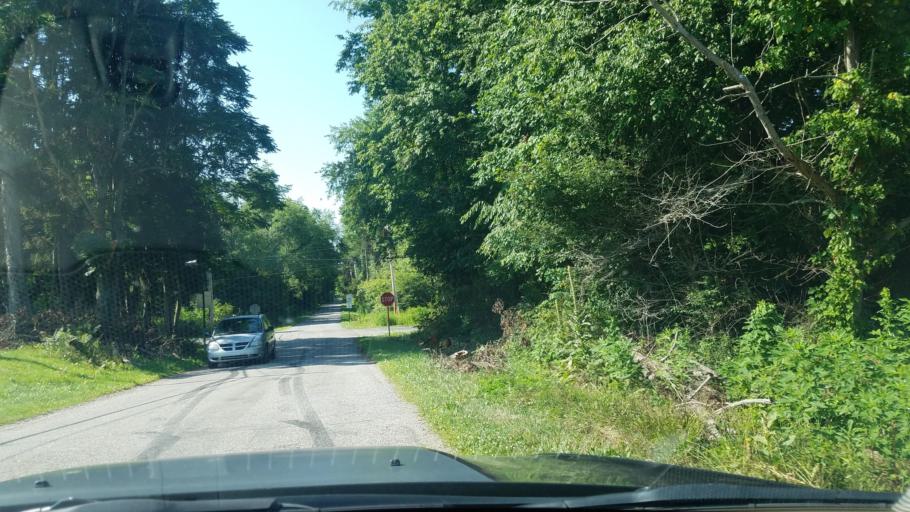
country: US
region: Ohio
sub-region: Trumbull County
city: Leavittsburg
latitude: 41.2613
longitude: -80.9249
